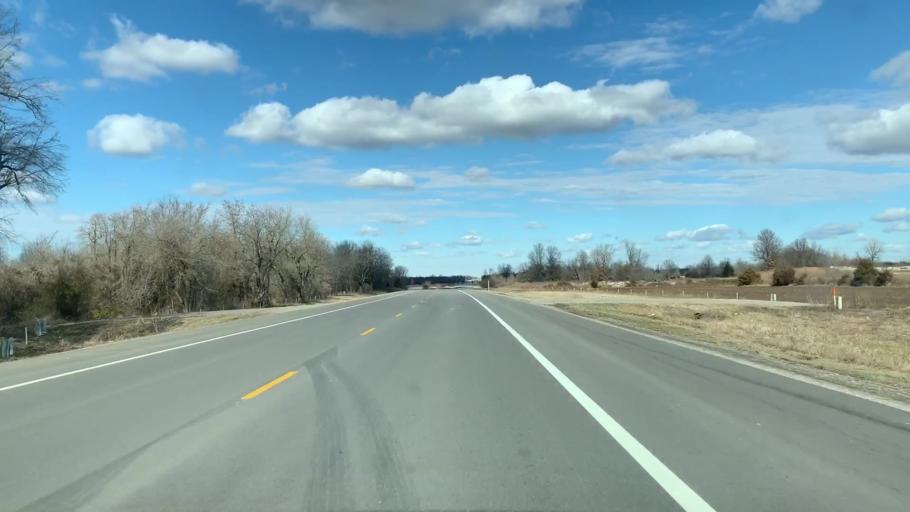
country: US
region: Kansas
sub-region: Cherokee County
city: Columbus
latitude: 37.2589
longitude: -94.8319
